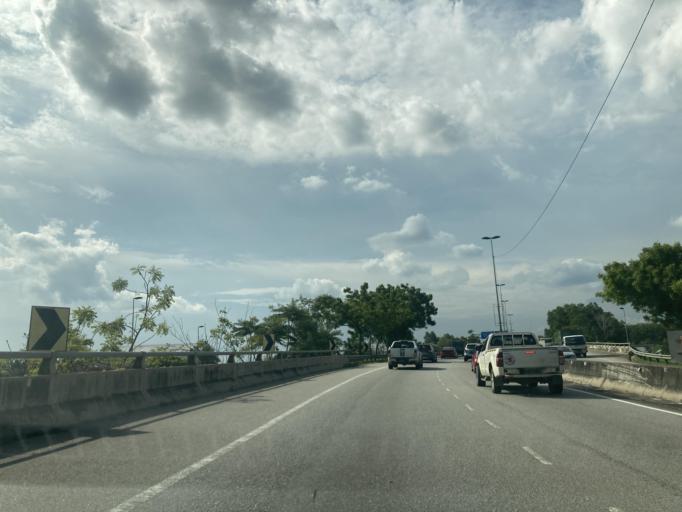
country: MY
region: Selangor
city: Kampung Baru Subang
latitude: 3.1356
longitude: 101.5529
